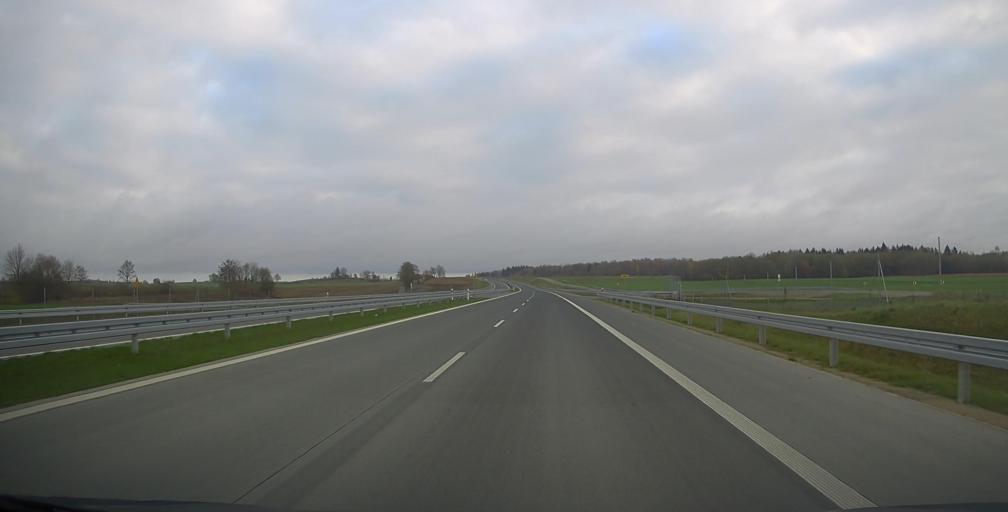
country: PL
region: Podlasie
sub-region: Powiat suwalski
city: Raczki
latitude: 53.9163
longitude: 22.7360
